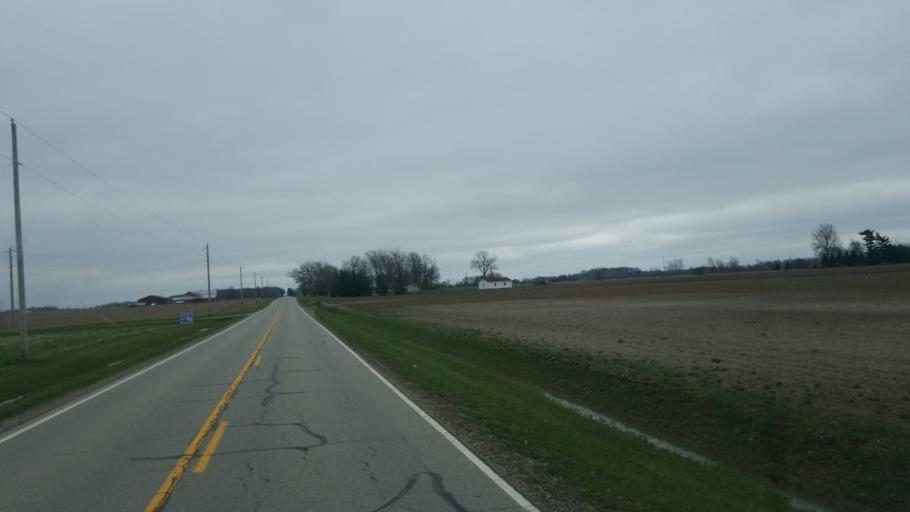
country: US
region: Ohio
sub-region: Crawford County
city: Bucyrus
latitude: 40.8191
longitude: -83.0682
